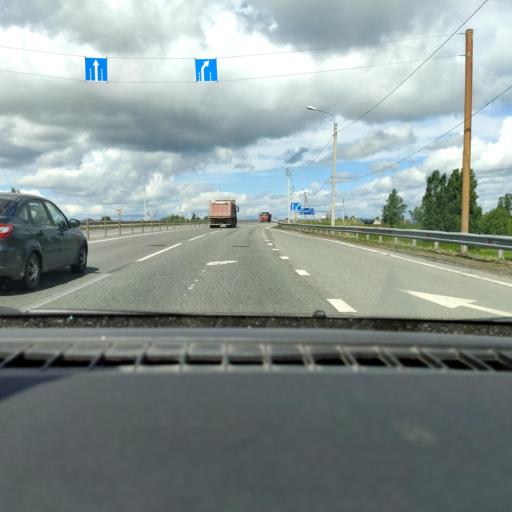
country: RU
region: Perm
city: Overyata
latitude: 58.0545
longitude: 55.8487
